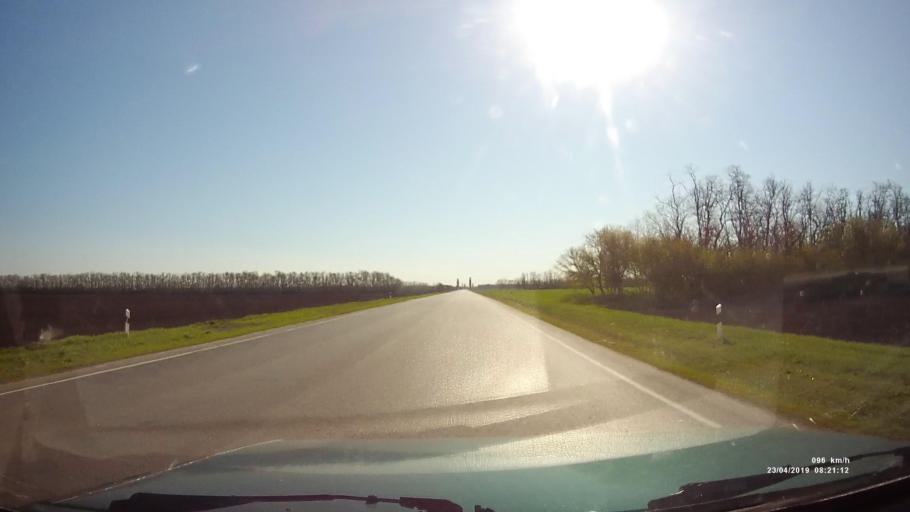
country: RU
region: Rostov
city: Tselina
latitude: 46.5361
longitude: 40.8853
